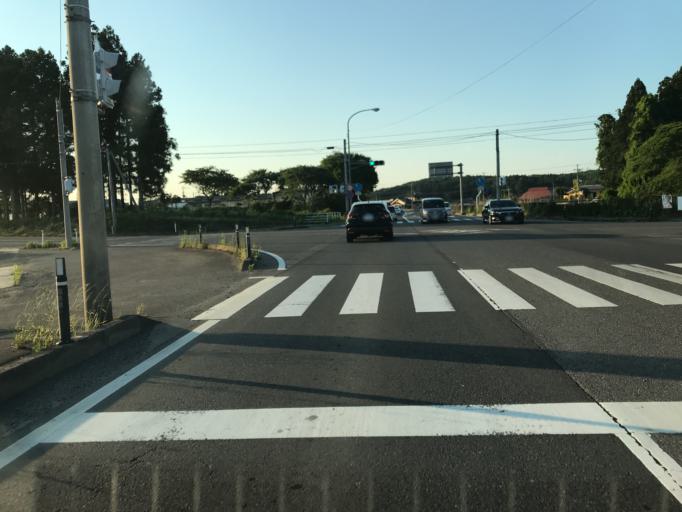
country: JP
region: Fukushima
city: Ishikawa
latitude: 37.1750
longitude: 140.3492
